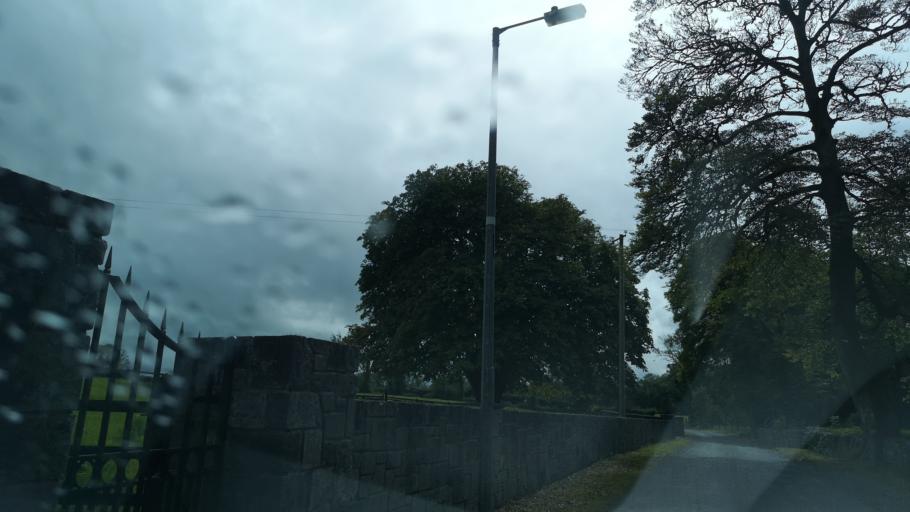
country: IE
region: Connaught
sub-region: County Galway
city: Loughrea
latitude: 53.3051
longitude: -8.5960
